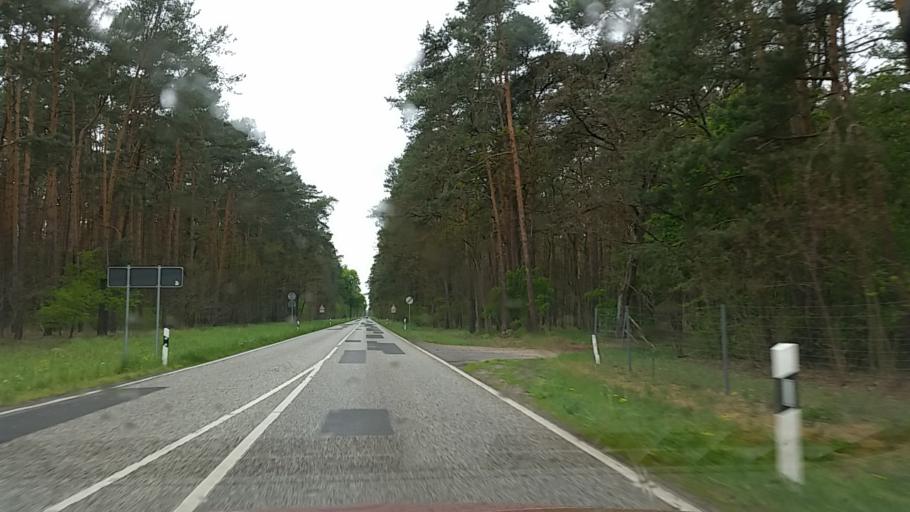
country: DE
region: Brandenburg
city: Storkow
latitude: 52.3255
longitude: 13.9395
